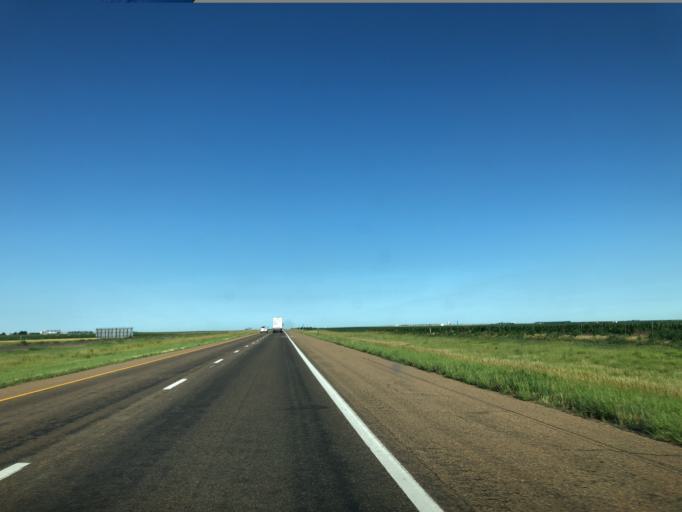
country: US
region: Kansas
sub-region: Thomas County
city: Colby
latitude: 39.3652
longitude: -101.1076
